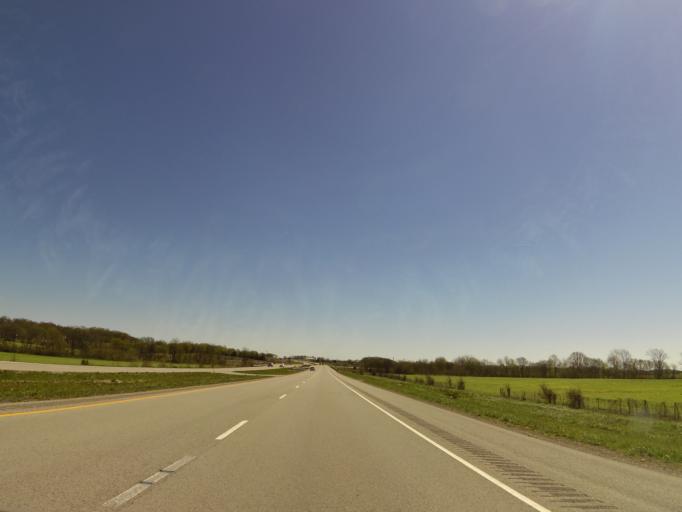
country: US
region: Kentucky
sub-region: Logan County
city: Auburn
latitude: 36.8920
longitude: -86.6480
